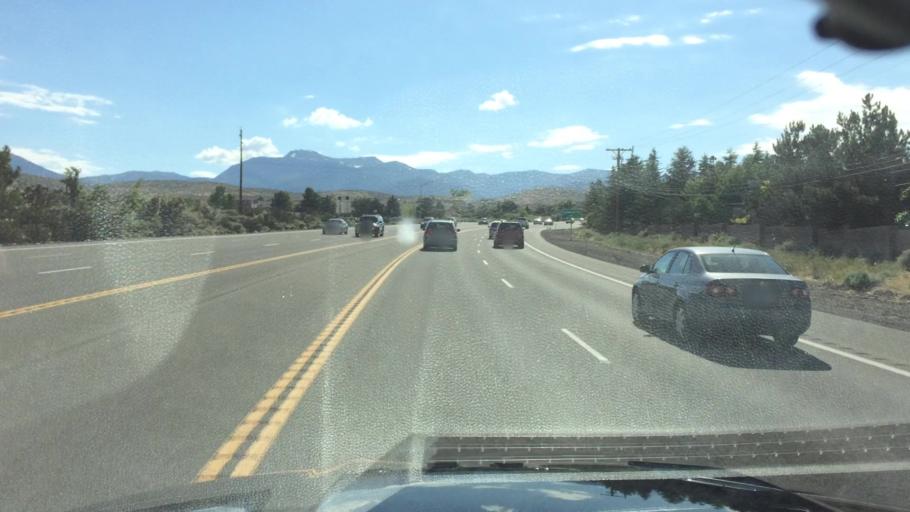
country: US
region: Nevada
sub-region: Washoe County
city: Sparks
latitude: 39.3918
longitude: -119.7700
